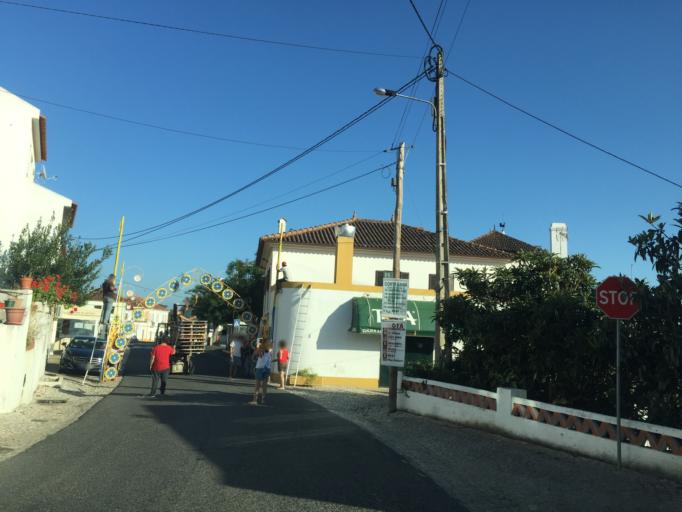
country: PT
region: Lisbon
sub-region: Alenquer
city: Alenquer
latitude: 39.1104
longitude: -8.9902
